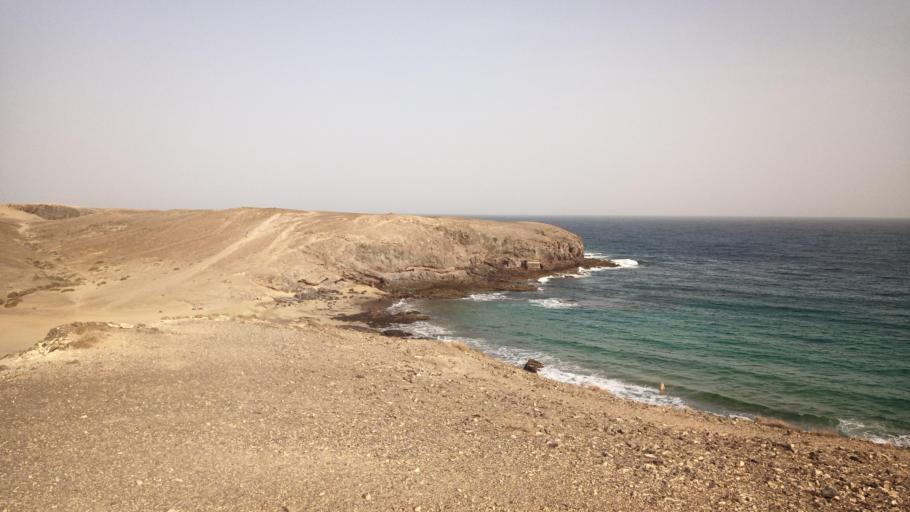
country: ES
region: Canary Islands
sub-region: Provincia de Las Palmas
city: Playa Blanca
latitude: 28.8437
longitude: -13.7822
